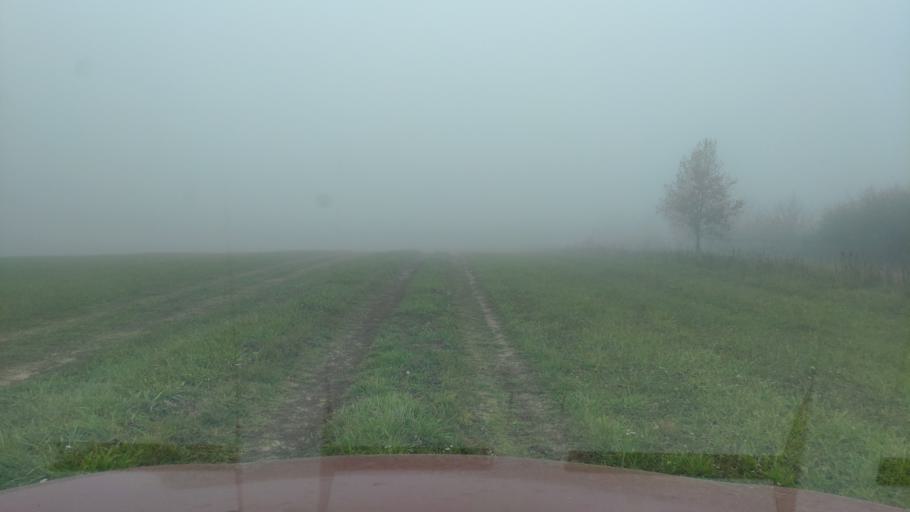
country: SK
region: Presovsky
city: Sabinov
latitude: 49.1460
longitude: 21.2221
